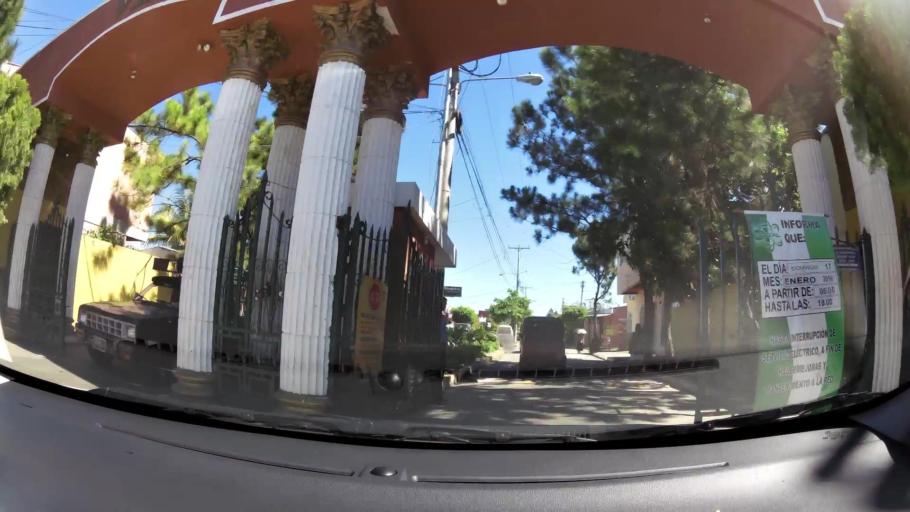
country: SV
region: La Libertad
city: San Juan Opico
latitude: 13.7924
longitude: -89.3590
